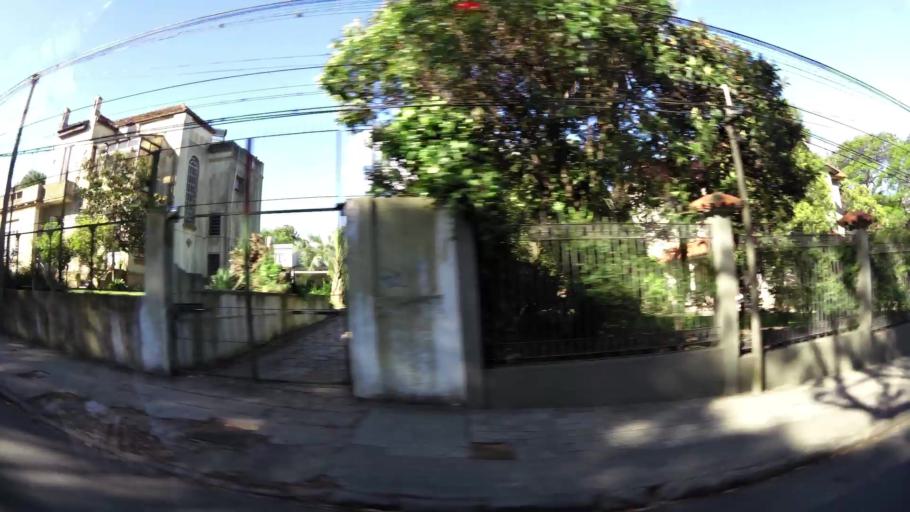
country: UY
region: Montevideo
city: Montevideo
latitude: -34.8537
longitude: -56.2075
